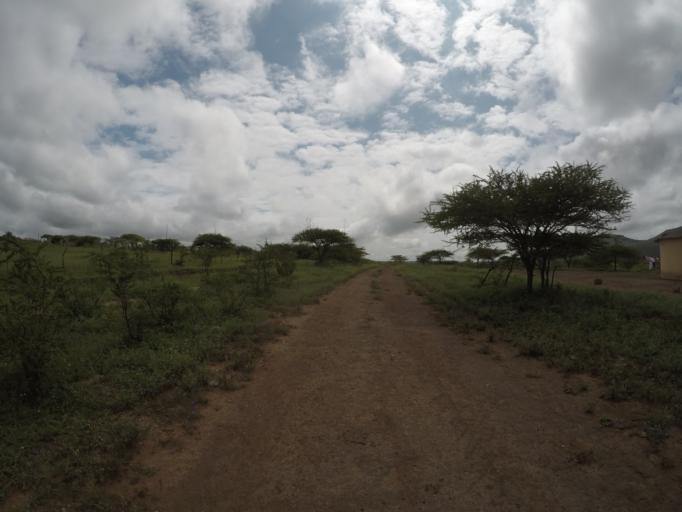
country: ZA
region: KwaZulu-Natal
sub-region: uThungulu District Municipality
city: Empangeni
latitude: -28.5840
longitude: 31.8528
